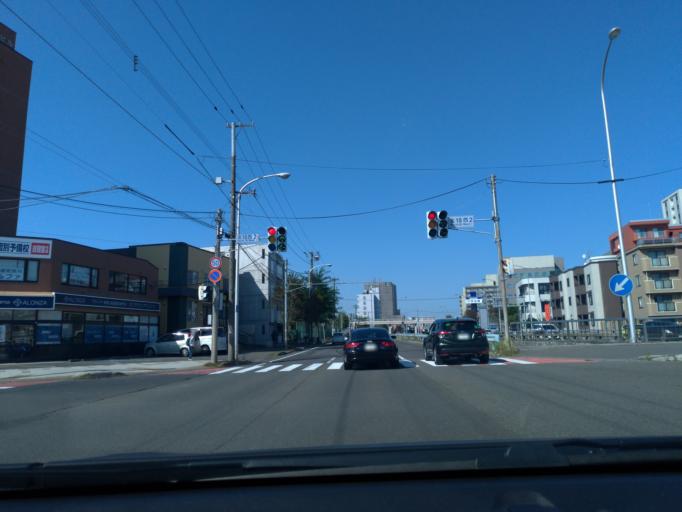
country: JP
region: Hokkaido
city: Sapporo
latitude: 43.0821
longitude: 141.3502
